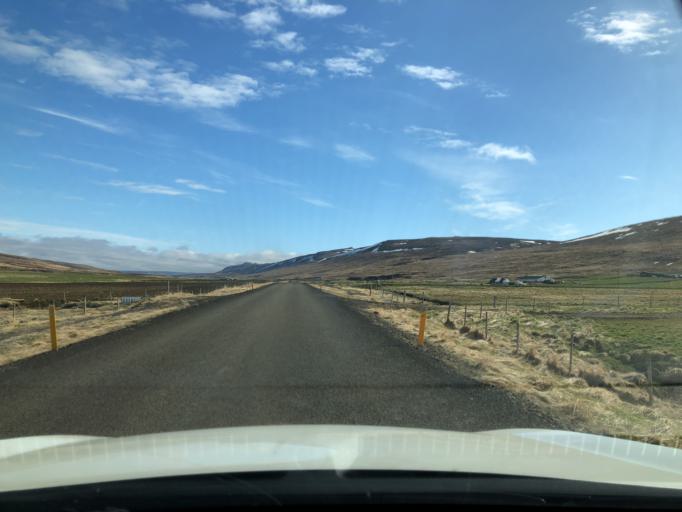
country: IS
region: West
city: Borgarnes
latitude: 65.1273
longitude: -21.6386
